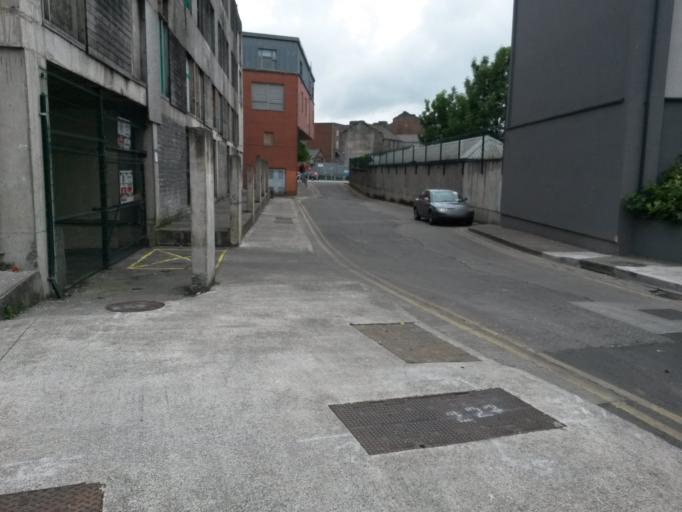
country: IE
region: Munster
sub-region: County Limerick
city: Luimneach
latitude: 52.6645
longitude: -8.6223
